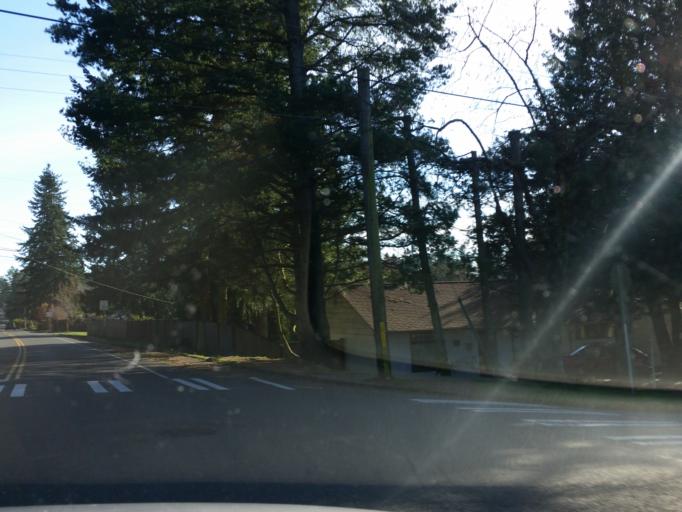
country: US
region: Washington
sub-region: Snohomish County
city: Mountlake Terrace
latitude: 47.7668
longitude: -122.3188
